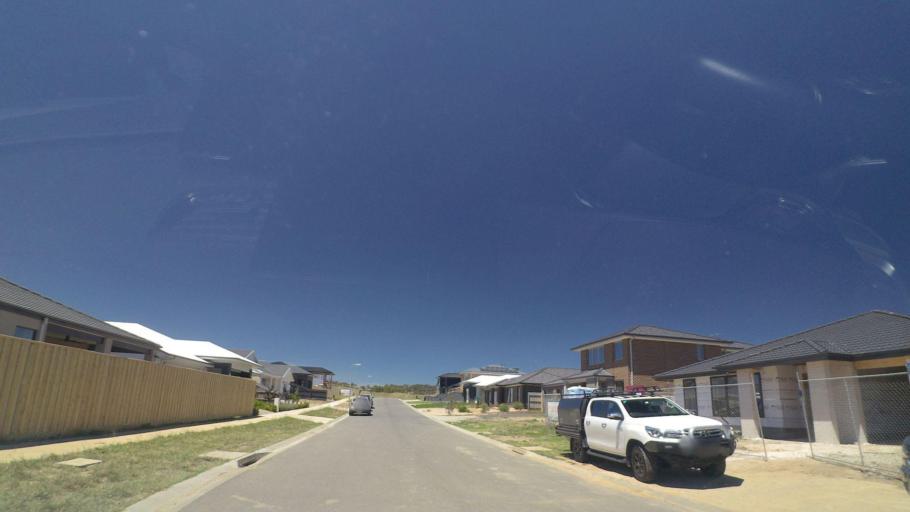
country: AU
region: Victoria
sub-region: Yarra Ranges
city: Lilydale
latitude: -37.7402
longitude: 145.3478
